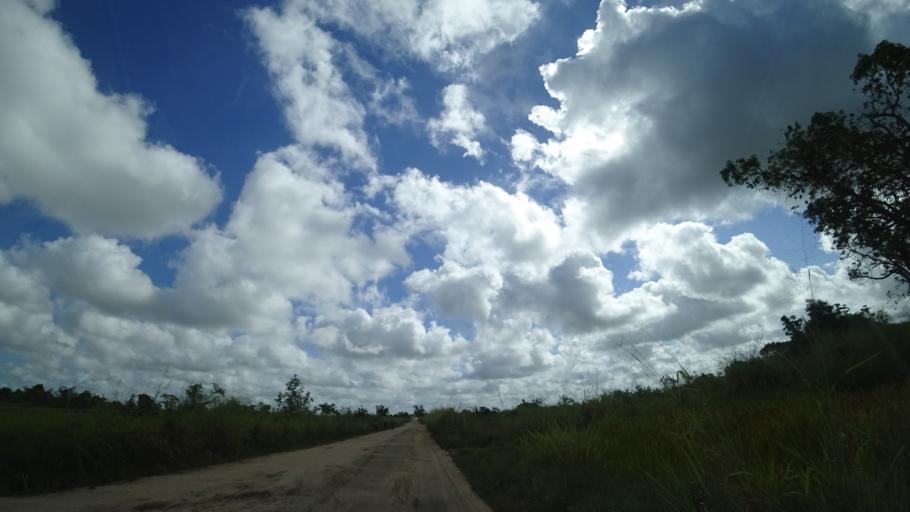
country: MZ
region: Sofala
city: Dondo
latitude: -19.4104
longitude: 34.7097
